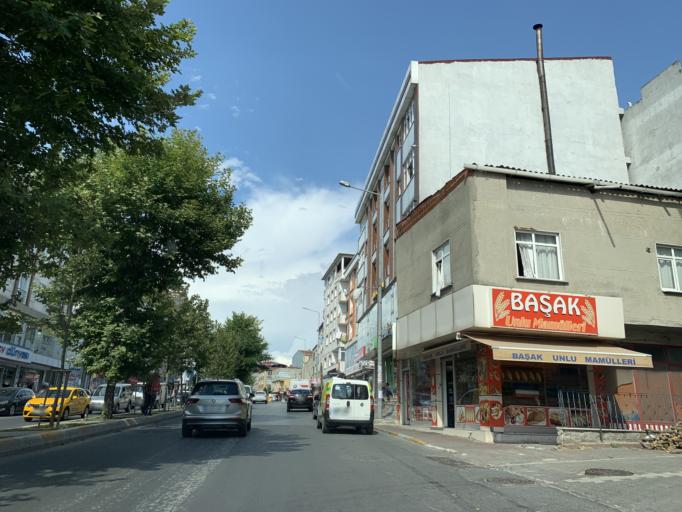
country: TR
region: Istanbul
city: Esenyurt
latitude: 41.0448
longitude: 28.6659
